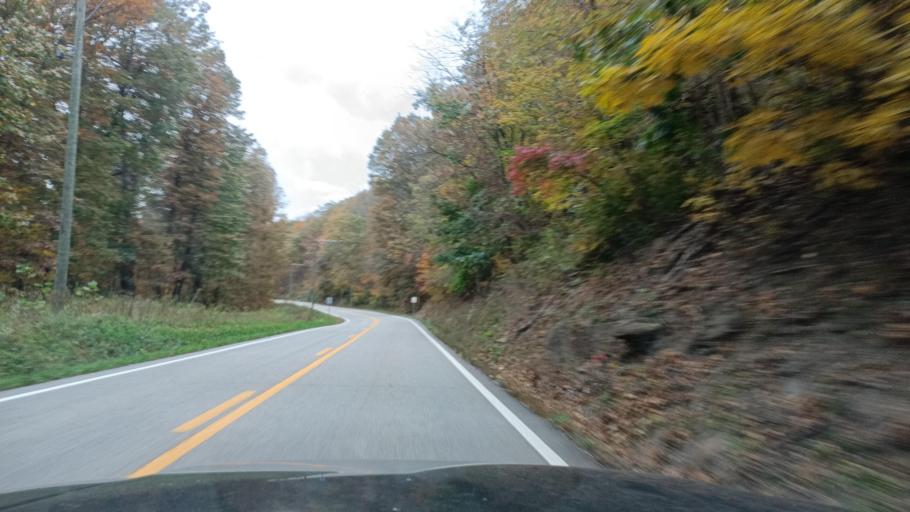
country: US
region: West Virginia
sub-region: Taylor County
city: Grafton
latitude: 39.3425
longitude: -79.9830
